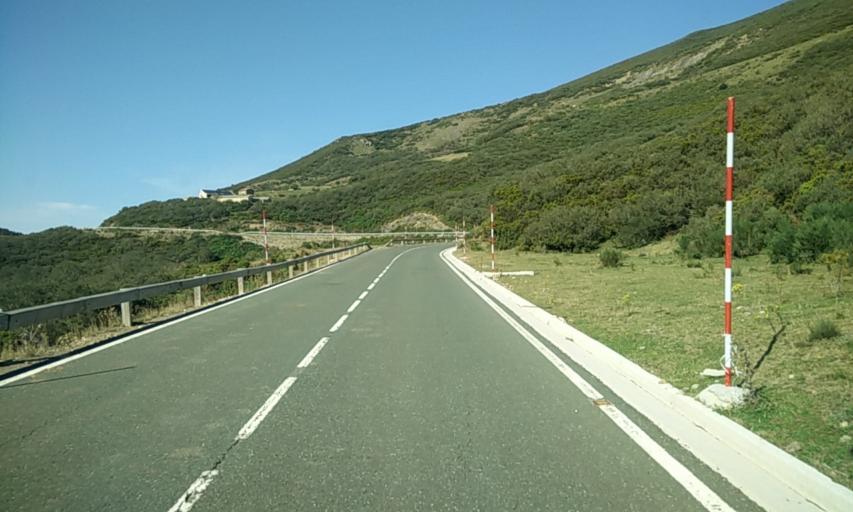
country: ES
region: Cantabria
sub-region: Provincia de Cantabria
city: Camaleno
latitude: 43.0693
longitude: -4.7566
